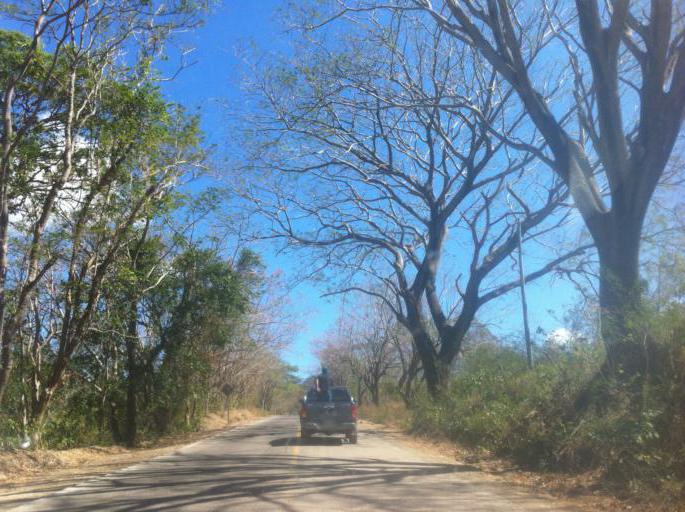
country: NI
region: Rivas
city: Tola
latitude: 11.3953
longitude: -85.9892
